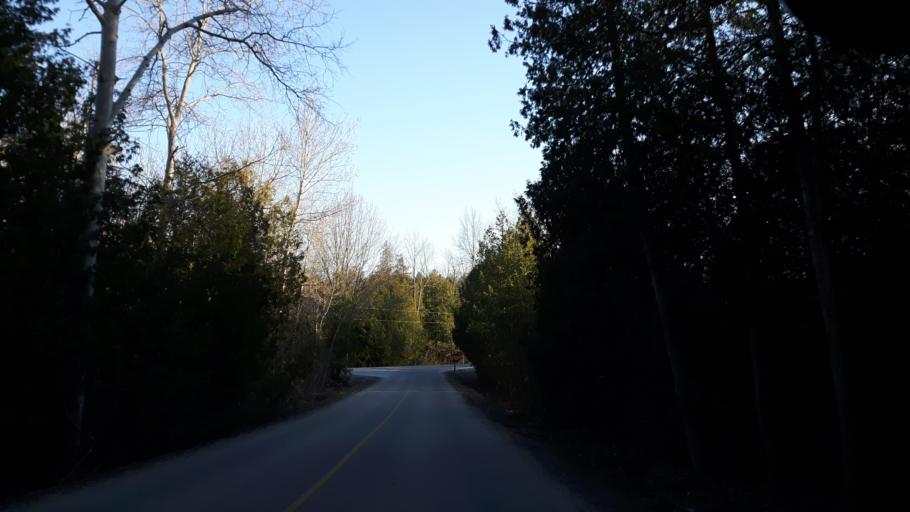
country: CA
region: Ontario
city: Bluewater
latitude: 43.5800
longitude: -81.6849
